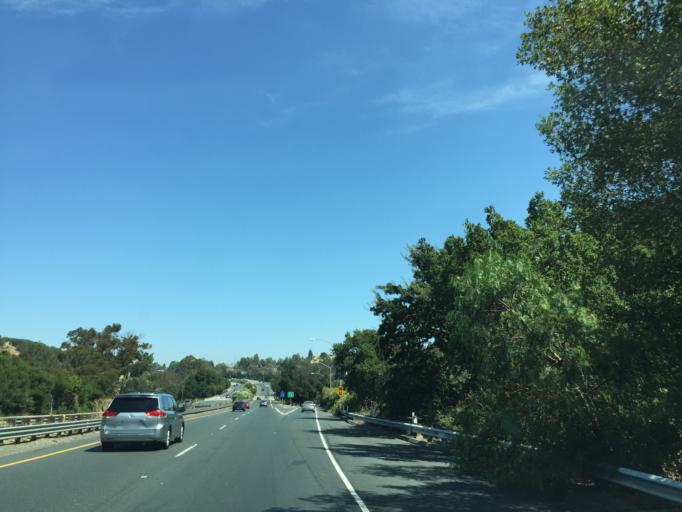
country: US
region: California
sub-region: Contra Costa County
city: Mountain View
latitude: 37.9899
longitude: -122.1339
